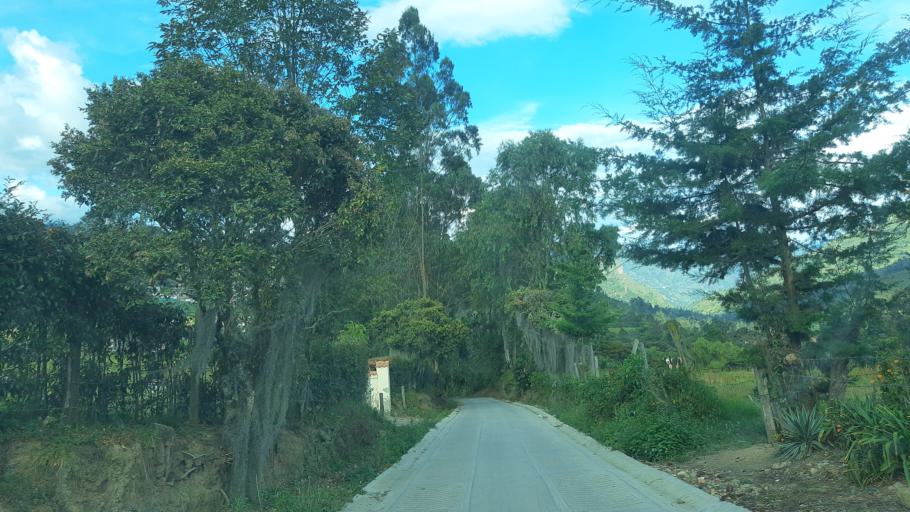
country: CO
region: Cundinamarca
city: Macheta
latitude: 5.0739
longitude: -73.6179
